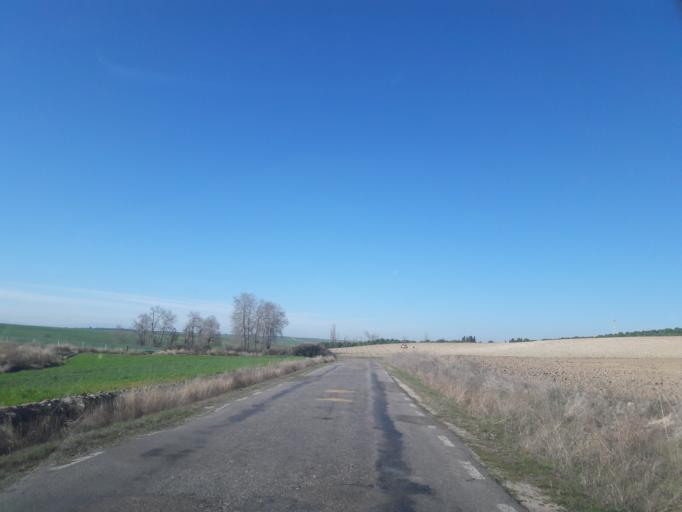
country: ES
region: Castille and Leon
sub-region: Provincia de Salamanca
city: Tordillos
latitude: 40.8628
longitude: -5.3404
